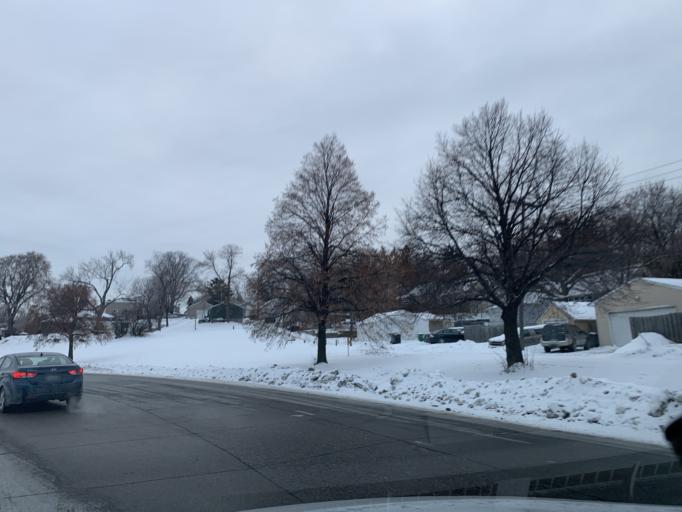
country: US
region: Minnesota
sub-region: Anoka County
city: Columbia Heights
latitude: 45.0239
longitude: -93.2856
